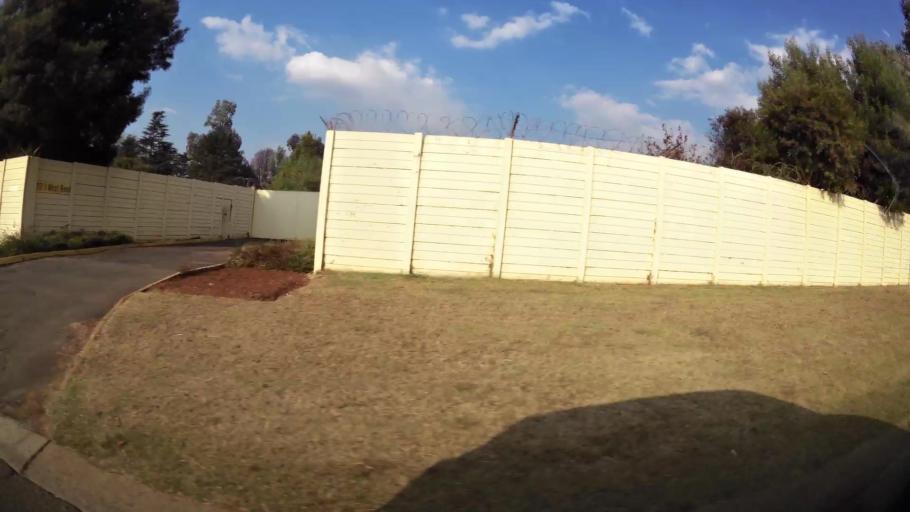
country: ZA
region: Gauteng
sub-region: Ekurhuleni Metropolitan Municipality
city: Benoni
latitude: -26.1038
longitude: 28.2761
